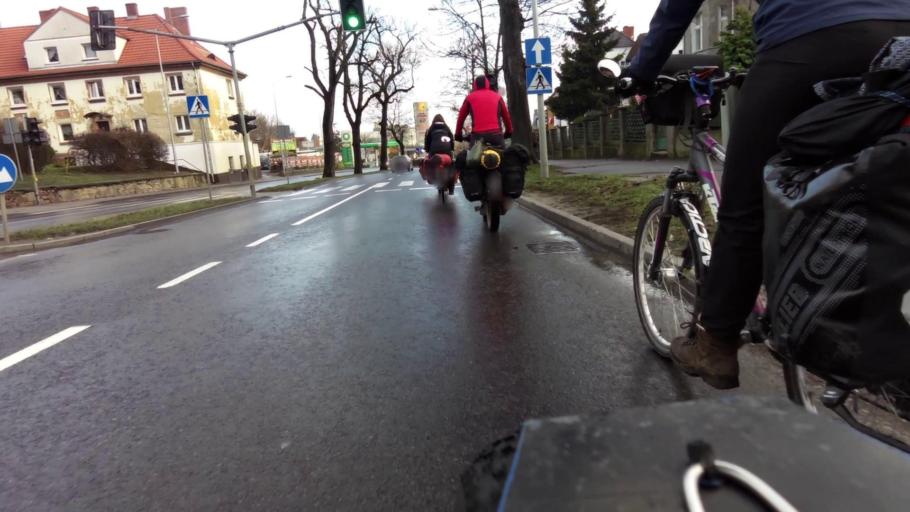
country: PL
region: Lubusz
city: Gorzow Wielkopolski
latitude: 52.7315
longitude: 15.2211
